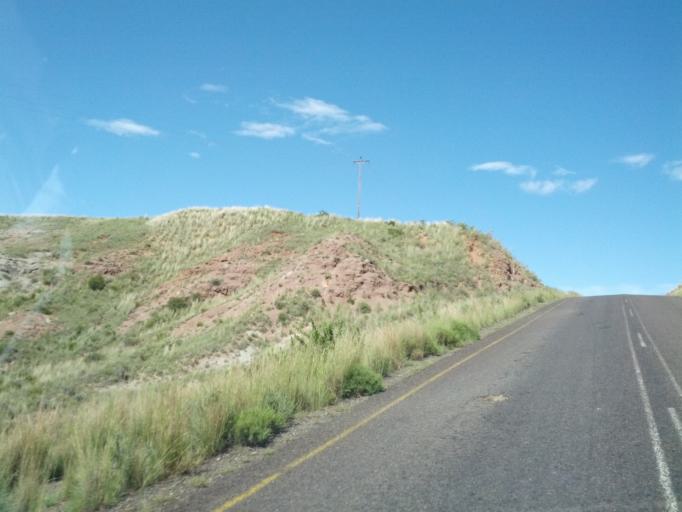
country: LS
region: Qacha's Nek
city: Qacha's Nek
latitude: -30.0725
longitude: 28.5743
